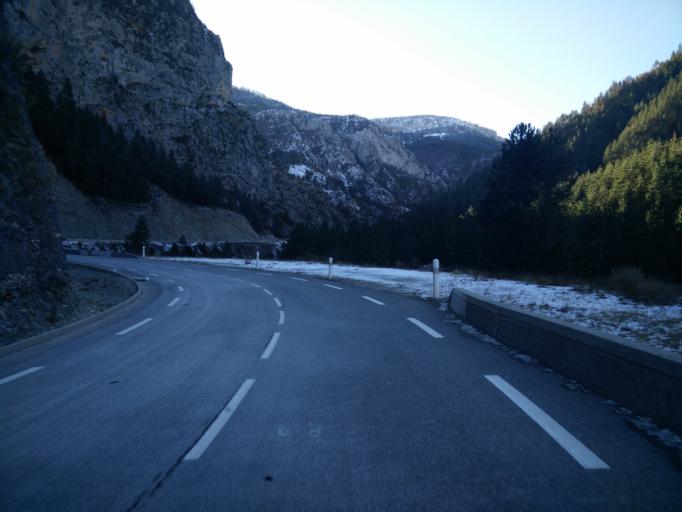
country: FR
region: Provence-Alpes-Cote d'Azur
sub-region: Departement des Alpes-de-Haute-Provence
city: Annot
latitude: 43.9455
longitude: 6.6895
